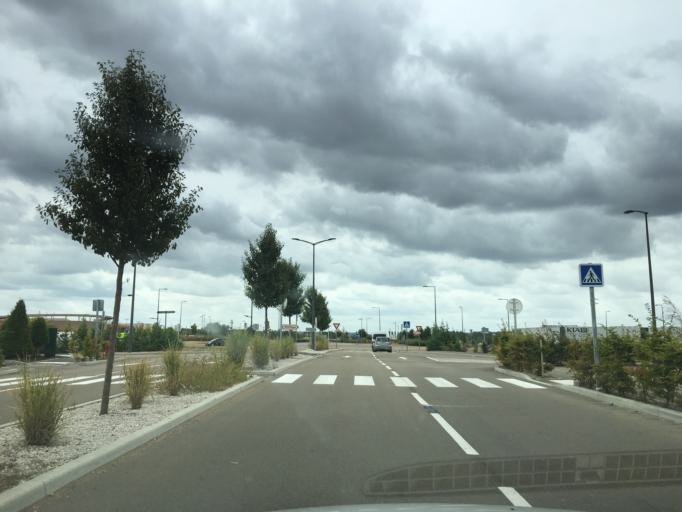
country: FR
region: Bourgogne
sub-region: Departement de l'Yonne
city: Maillot
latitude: 48.1748
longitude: 3.2899
